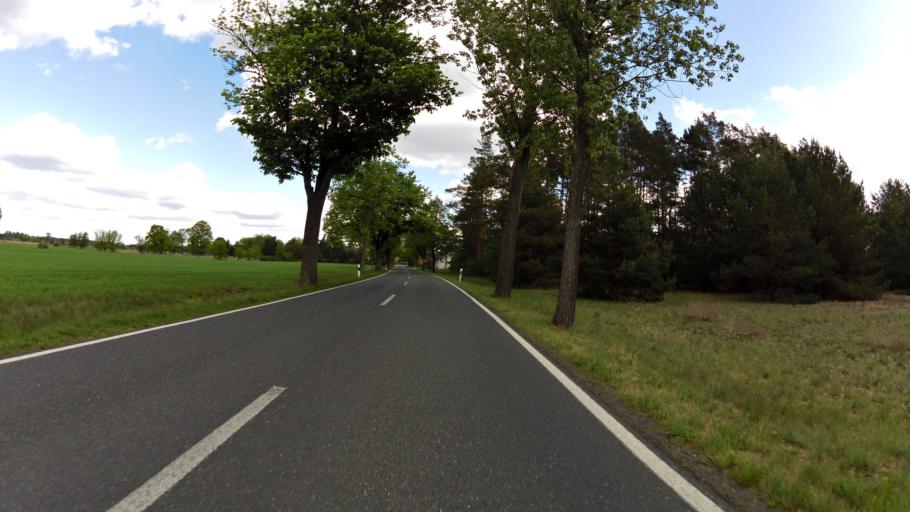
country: DE
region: Brandenburg
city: Schlepzig
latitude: 52.0938
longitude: 13.8996
